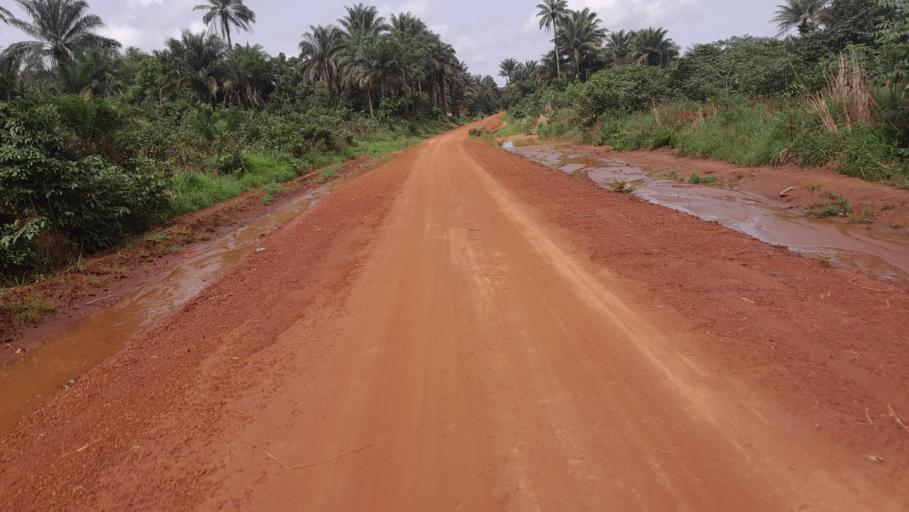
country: GN
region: Boke
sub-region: Boffa
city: Boffa
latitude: 10.0344
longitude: -13.8760
